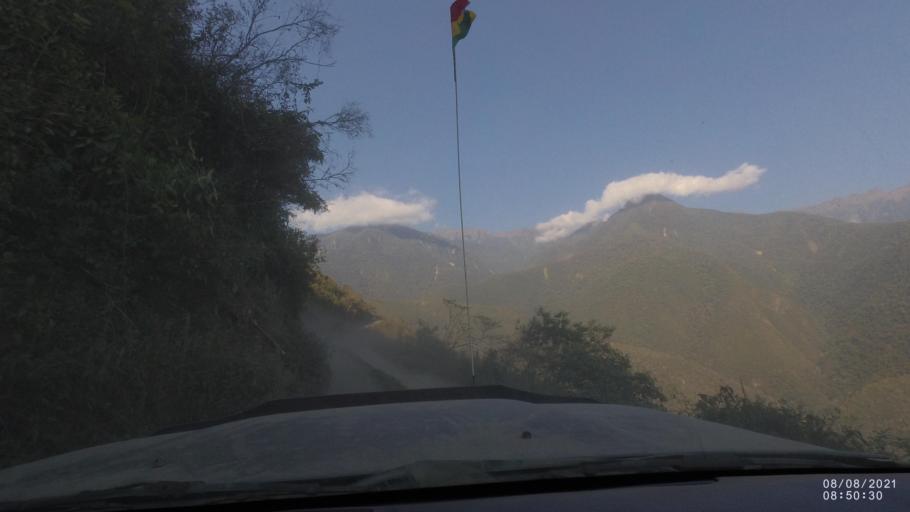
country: BO
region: La Paz
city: Quime
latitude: -16.5353
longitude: -66.7598
